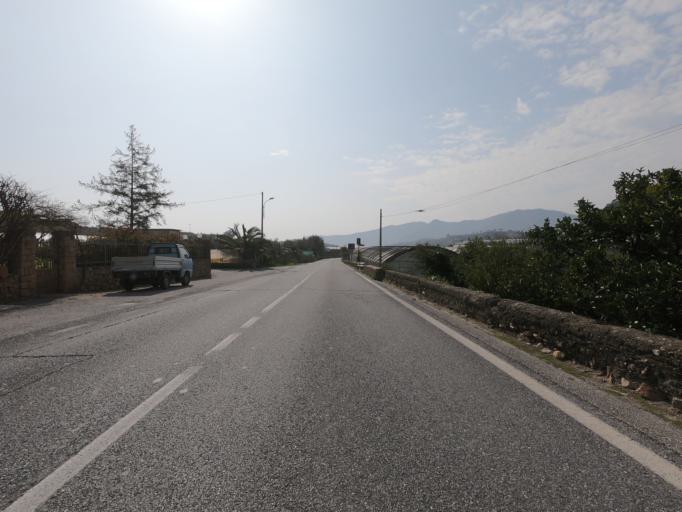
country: IT
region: Liguria
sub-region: Provincia di Savona
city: Cisano
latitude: 44.0816
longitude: 8.1552
